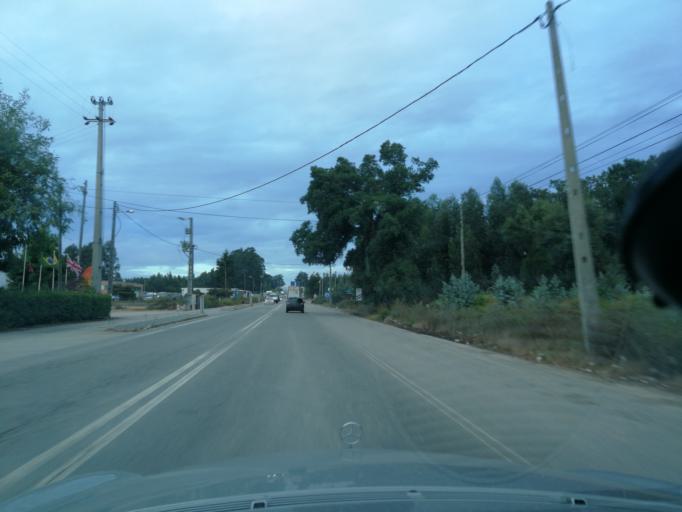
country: PT
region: Aveiro
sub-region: Albergaria-A-Velha
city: Albergaria-a-Velha
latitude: 40.6694
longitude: -8.4743
